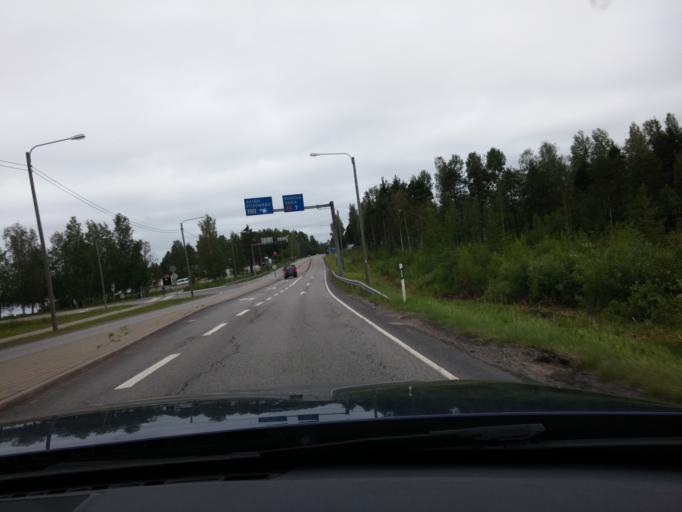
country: FI
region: Central Finland
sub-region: Saarijaervi-Viitasaari
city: Saarijaervi
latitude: 62.6975
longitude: 25.2869
